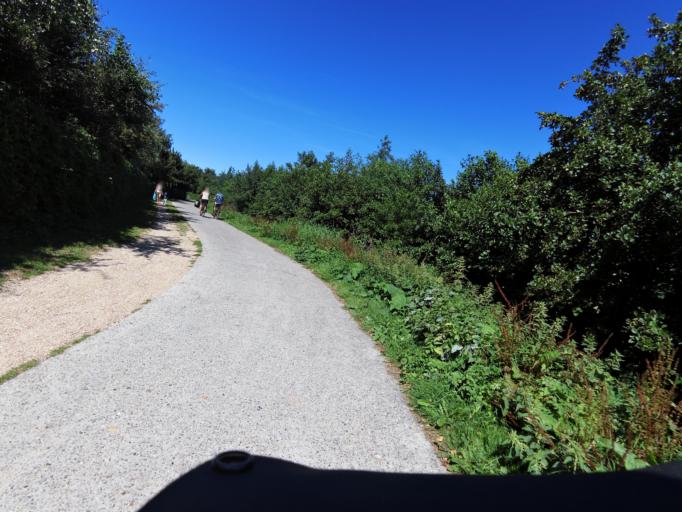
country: NL
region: Zeeland
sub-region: Schouwen-Duiveland
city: Haamstede
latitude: 51.7191
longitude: 3.7275
